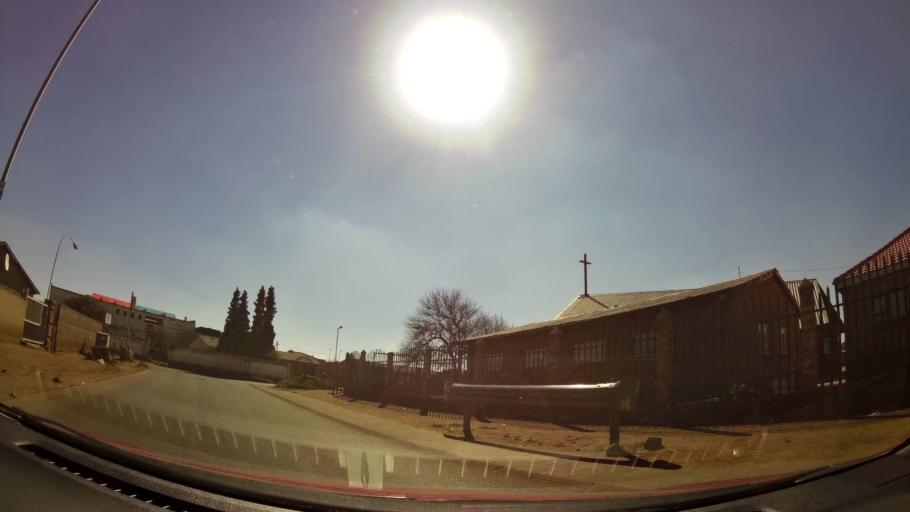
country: ZA
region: Gauteng
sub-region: City of Johannesburg Metropolitan Municipality
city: Soweto
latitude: -26.2389
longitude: 27.8396
